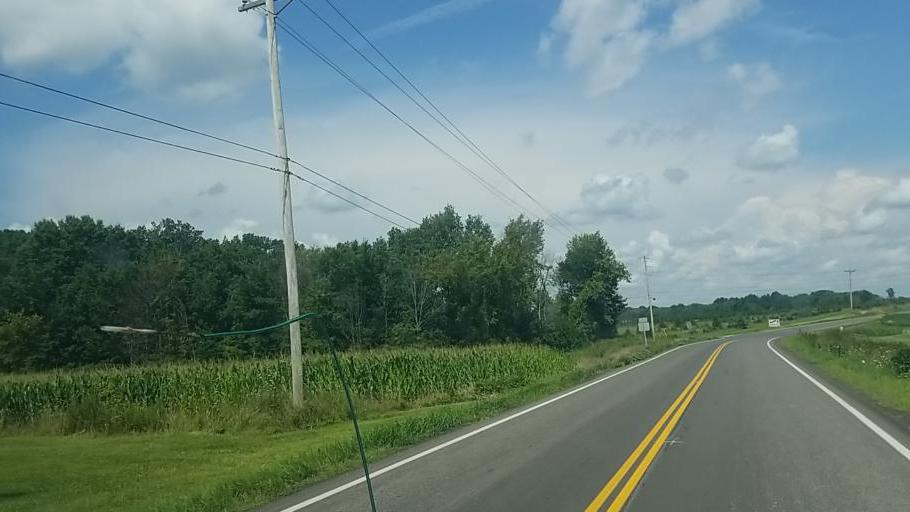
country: US
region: Ohio
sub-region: Wayne County
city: West Salem
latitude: 40.9514
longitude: -82.0840
